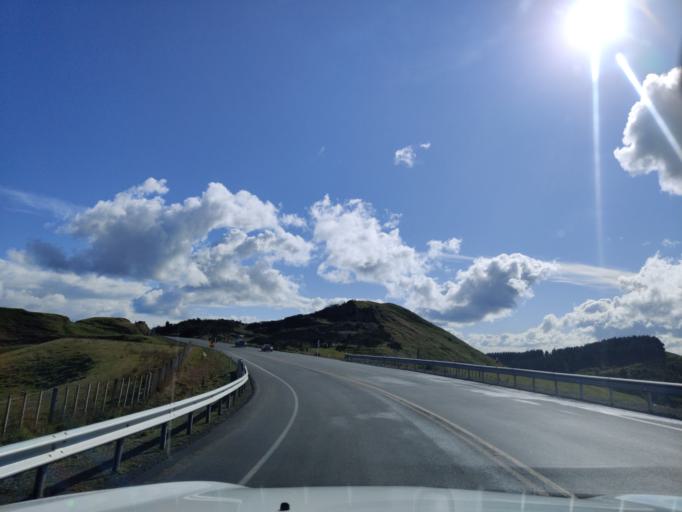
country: NZ
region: Manawatu-Wanganui
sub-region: Palmerston North City
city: Palmerston North
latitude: -40.2919
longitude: 175.8037
